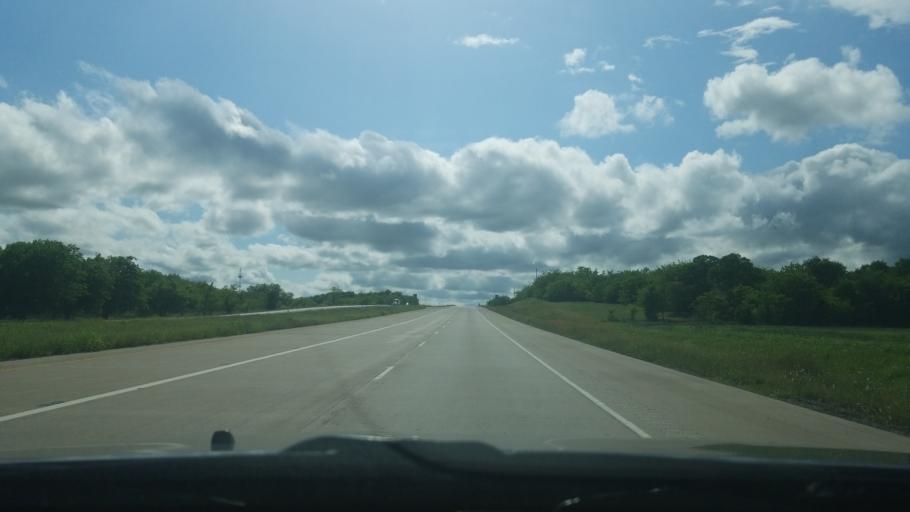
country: US
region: Texas
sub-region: Wise County
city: Decatur
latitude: 33.2458
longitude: -97.4577
